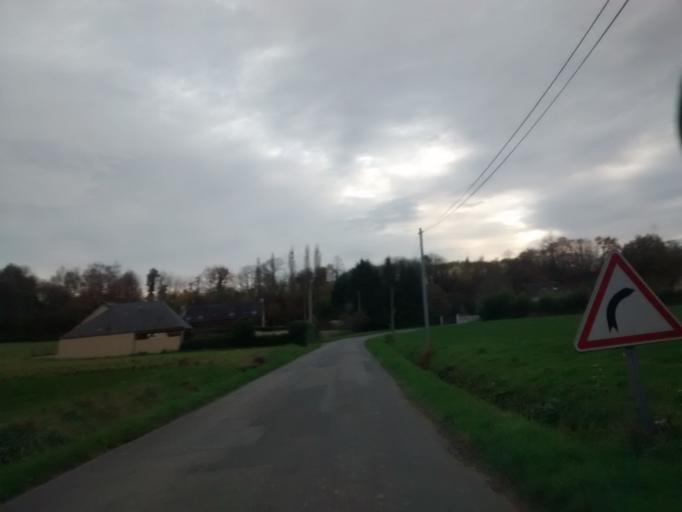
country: FR
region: Brittany
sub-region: Departement d'Ille-et-Vilaine
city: Acigne
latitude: 48.1199
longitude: -1.5505
